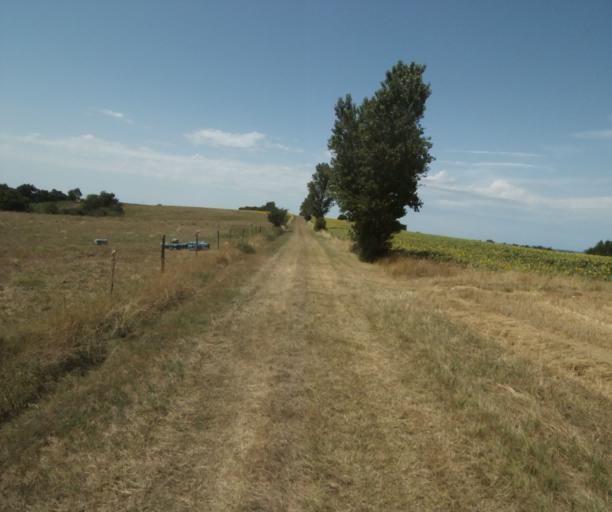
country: FR
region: Midi-Pyrenees
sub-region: Departement de la Haute-Garonne
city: Saint-Felix-Lauragais
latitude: 43.4457
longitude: 1.8628
